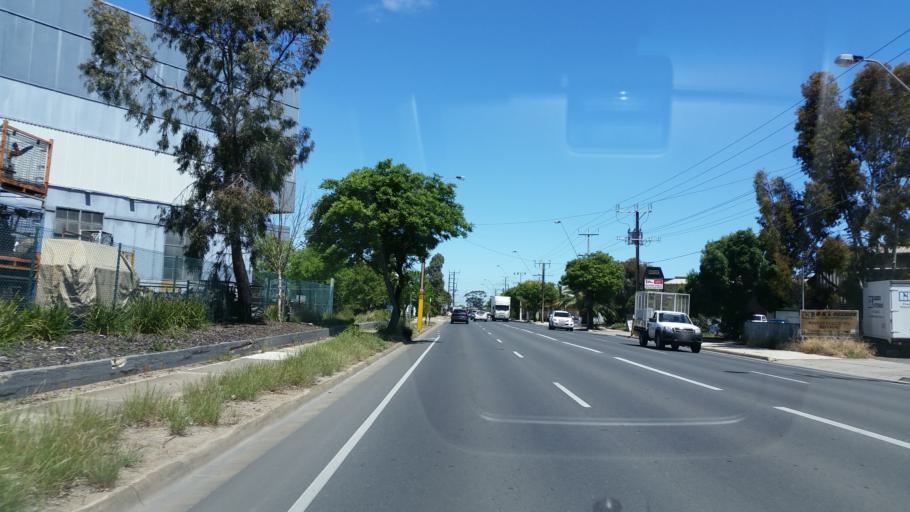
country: AU
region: South Australia
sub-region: Charles Sturt
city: Albert Park
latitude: -34.8727
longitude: 138.5285
